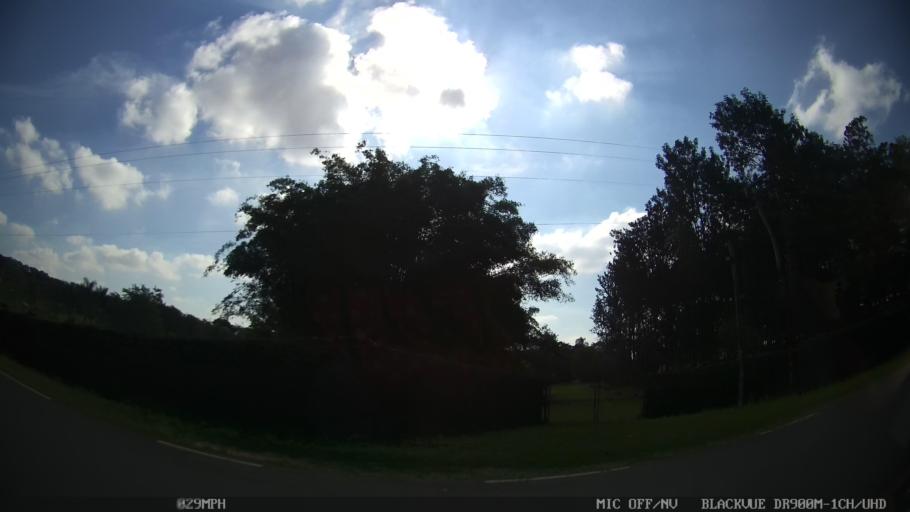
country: BR
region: Sao Paulo
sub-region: Indaiatuba
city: Indaiatuba
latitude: -22.9940
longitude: -47.1898
